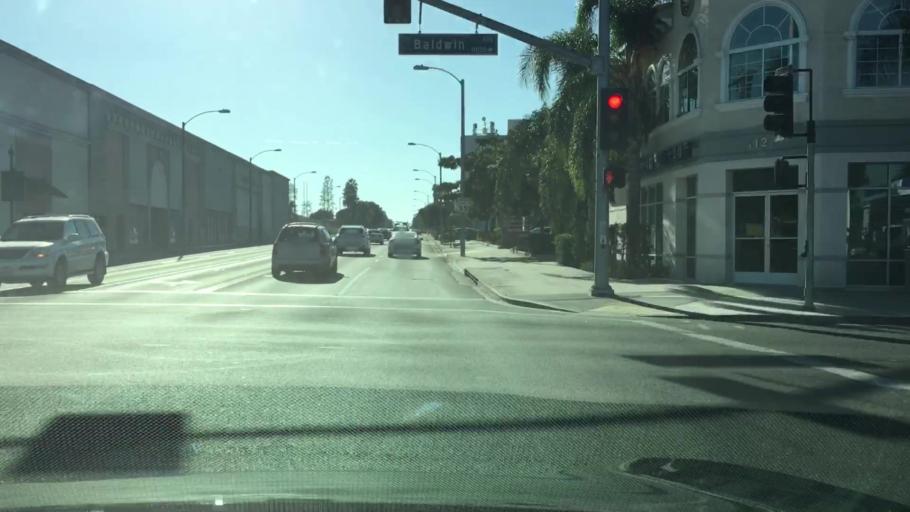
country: US
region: California
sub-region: Los Angeles County
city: Temple City
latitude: 34.1262
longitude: -118.0549
